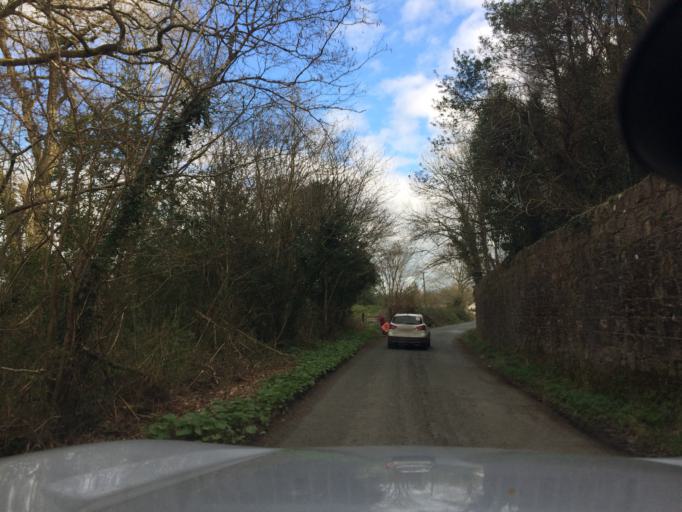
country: IE
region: Munster
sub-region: Waterford
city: Portlaw
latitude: 52.2832
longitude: -7.3196
